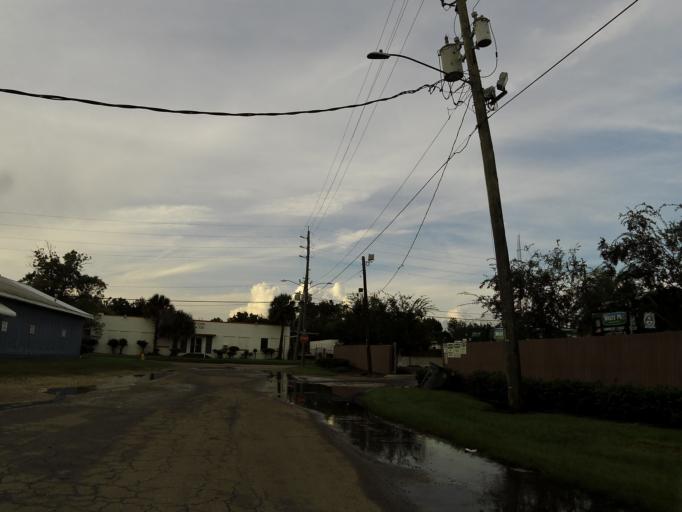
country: US
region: Florida
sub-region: Duval County
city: Jacksonville
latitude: 30.3296
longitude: -81.7039
